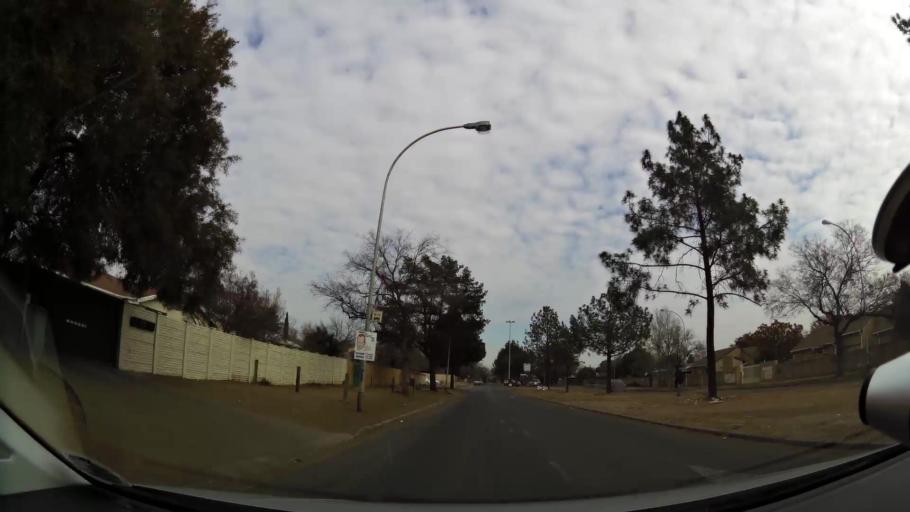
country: ZA
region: Orange Free State
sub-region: Mangaung Metropolitan Municipality
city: Bloemfontein
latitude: -29.1312
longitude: 26.1846
